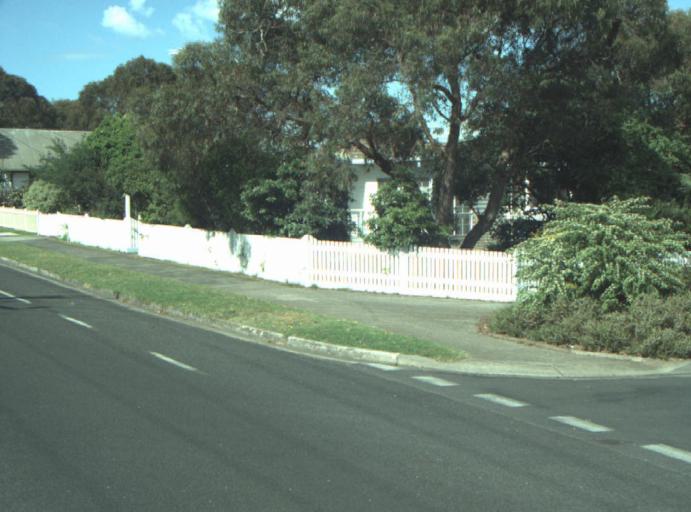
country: AU
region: Victoria
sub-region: Greater Geelong
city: Leopold
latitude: -38.2643
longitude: 144.5232
